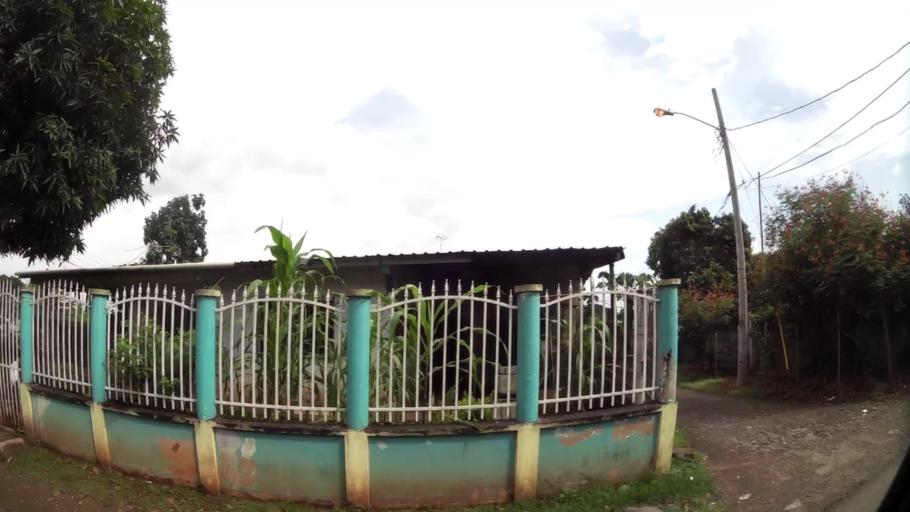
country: PA
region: Panama
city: Tocumen
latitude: 9.1004
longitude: -79.3670
